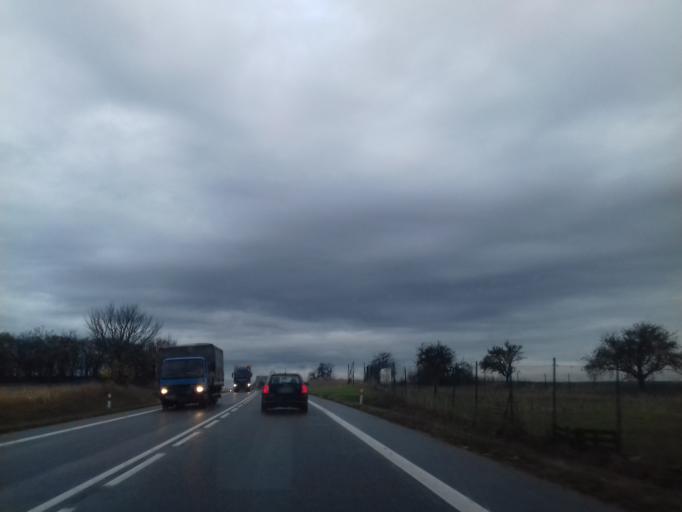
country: CZ
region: Pardubicky
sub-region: Okres Pardubice
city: Vysoke Myto
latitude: 49.9171
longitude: 16.1934
